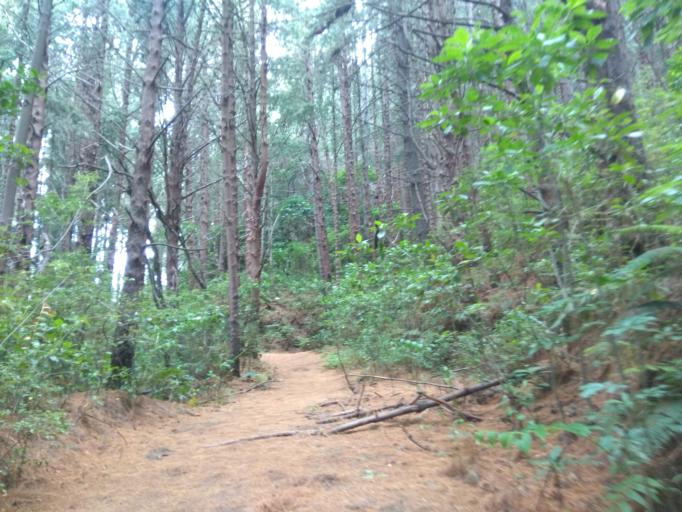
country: CR
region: Cartago
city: Cot
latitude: 9.9600
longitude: -83.8824
